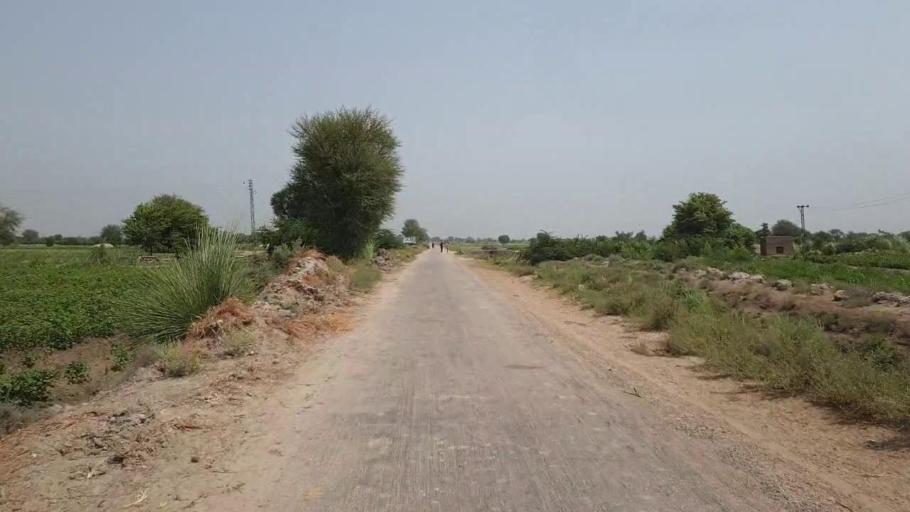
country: PK
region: Sindh
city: Nawabshah
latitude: 26.2684
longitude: 68.3163
